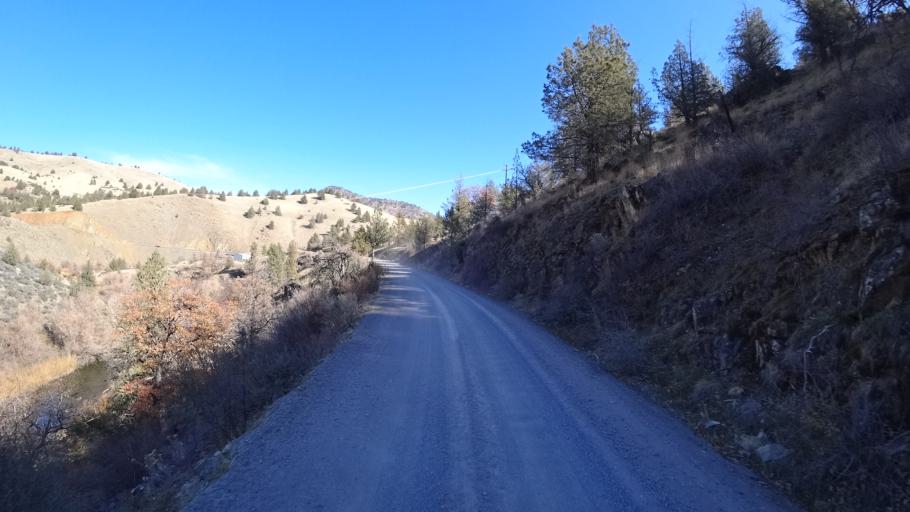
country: US
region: California
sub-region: Siskiyou County
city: Yreka
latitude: 41.7815
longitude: -122.6023
